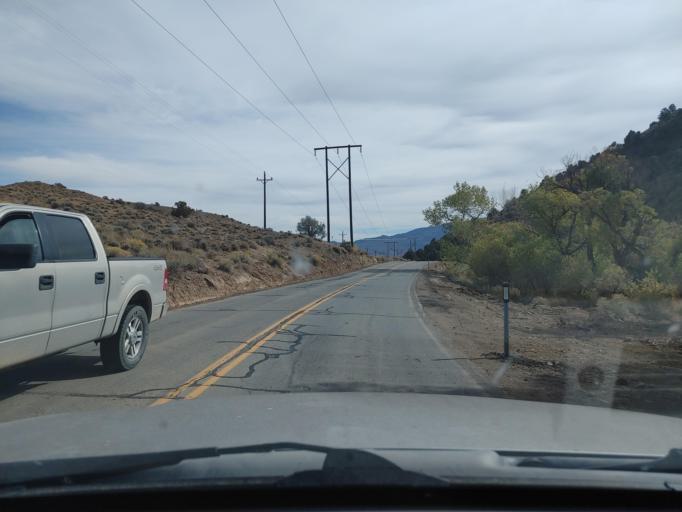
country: US
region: Nevada
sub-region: Storey County
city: Virginia City
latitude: 39.3162
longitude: -119.5843
